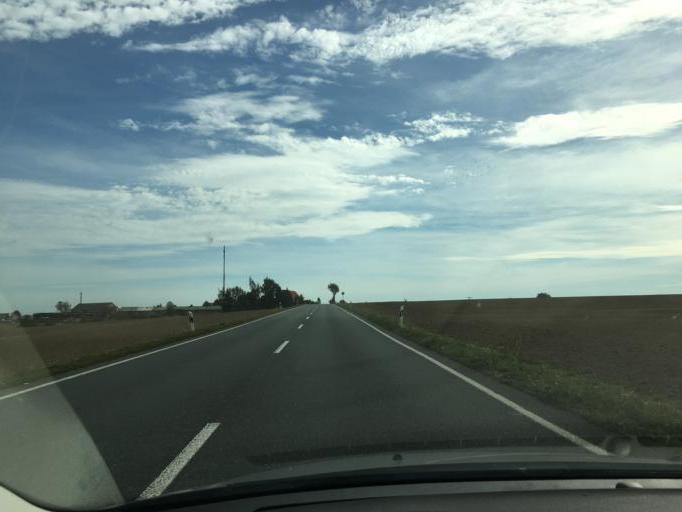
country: DE
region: Saxony
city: Lommatzsch
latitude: 51.2168
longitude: 13.3696
